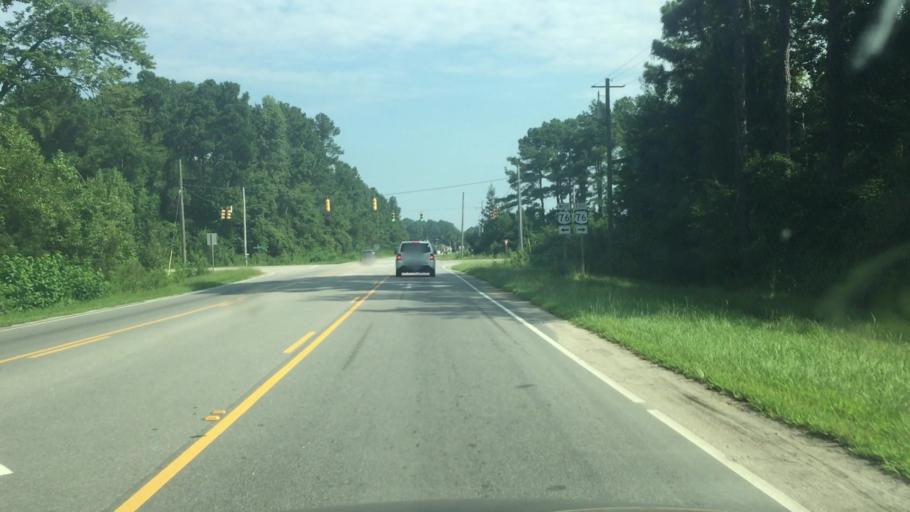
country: US
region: North Carolina
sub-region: Columbus County
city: Chadbourn
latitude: 34.3349
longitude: -78.8268
